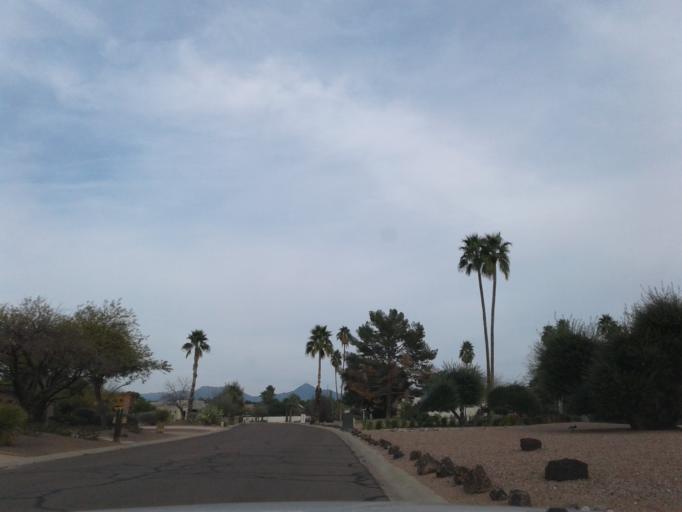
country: US
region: Arizona
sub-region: Maricopa County
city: Paradise Valley
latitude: 33.5770
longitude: -111.9375
